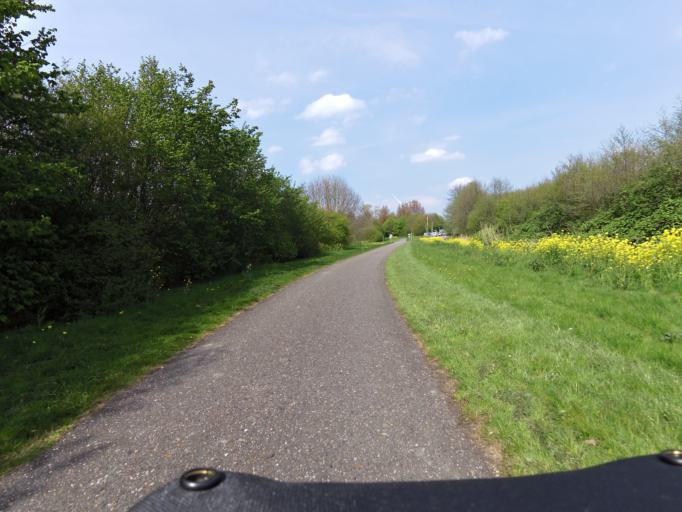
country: NL
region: South Holland
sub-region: Gemeente Brielle
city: Brielle
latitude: 51.8928
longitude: 4.2089
